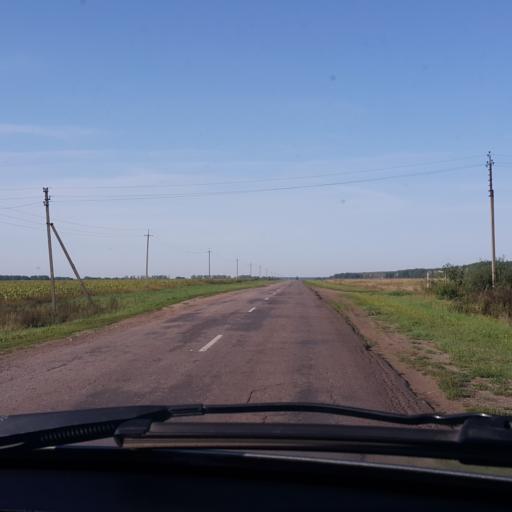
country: RU
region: Tambov
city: Novaya Lyada
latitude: 52.7689
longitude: 41.7428
